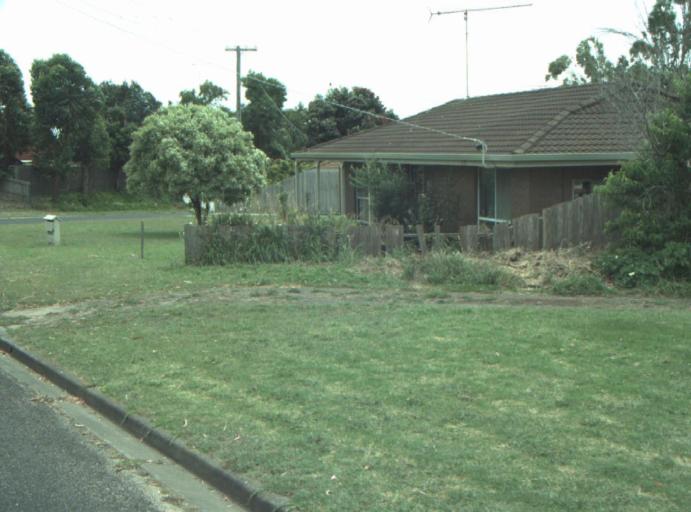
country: AU
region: Victoria
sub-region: Greater Geelong
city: Clifton Springs
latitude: -38.1605
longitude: 144.5524
